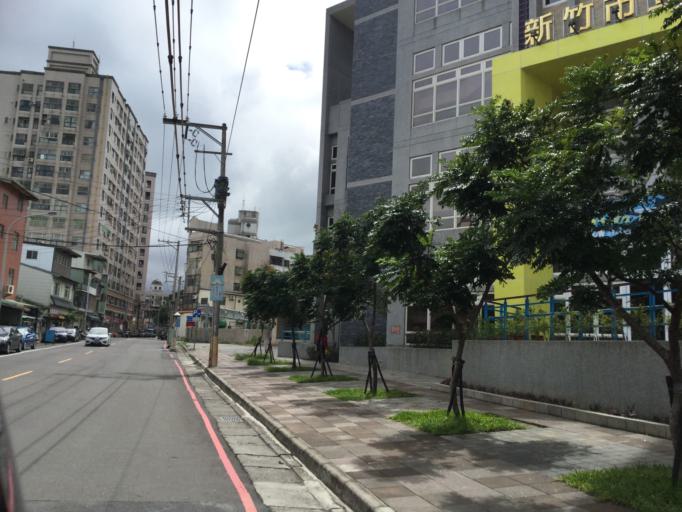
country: TW
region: Taiwan
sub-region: Hsinchu
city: Hsinchu
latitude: 24.7800
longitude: 121.0244
